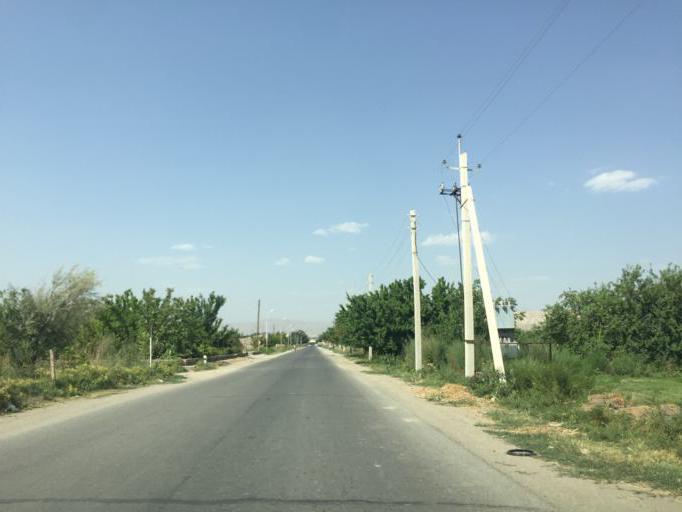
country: AM
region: Ararat
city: Shahumyan
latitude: 39.8939
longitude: 44.5959
